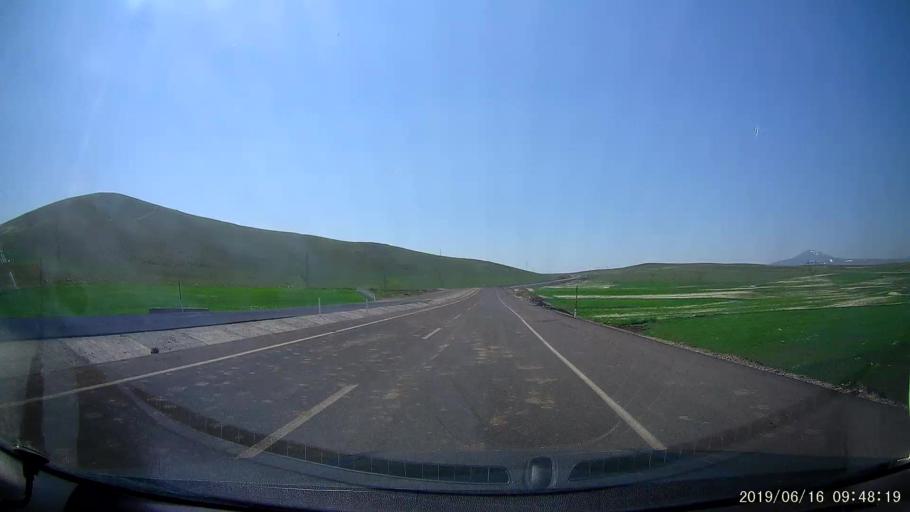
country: TR
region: Kars
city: Digor
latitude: 40.4349
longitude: 43.3515
